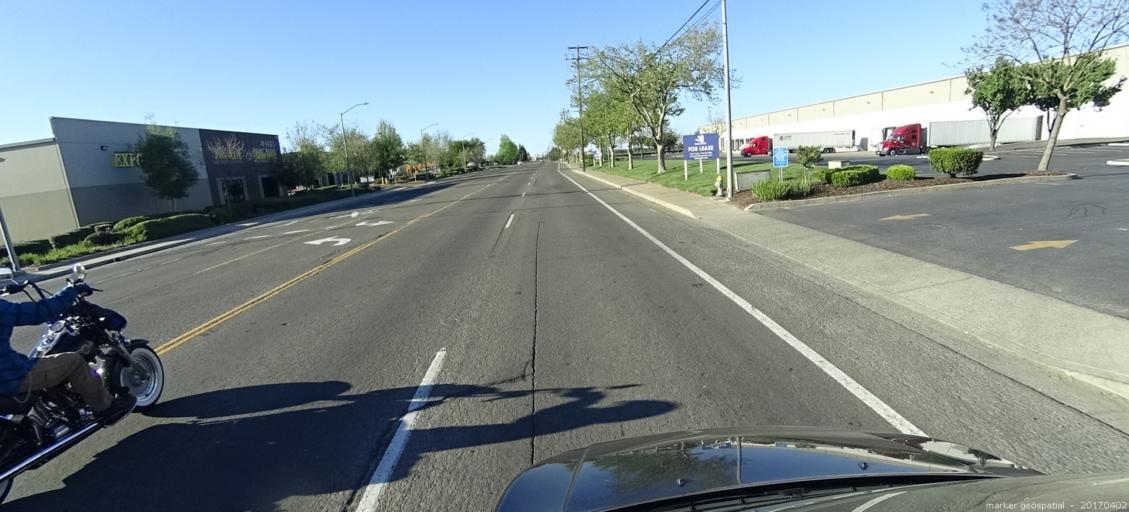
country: US
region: California
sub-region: Sacramento County
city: Rosemont
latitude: 38.5324
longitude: -121.3907
